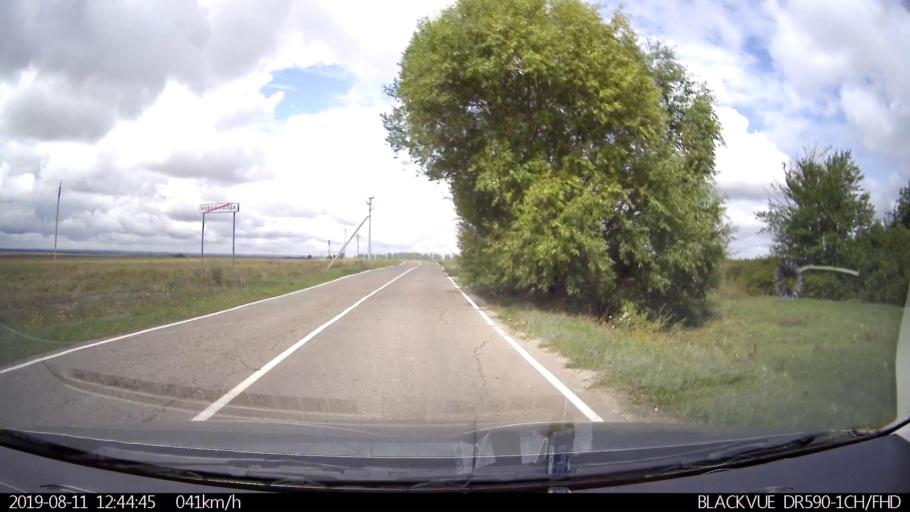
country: RU
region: Ulyanovsk
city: Ignatovka
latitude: 53.8562
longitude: 47.7335
